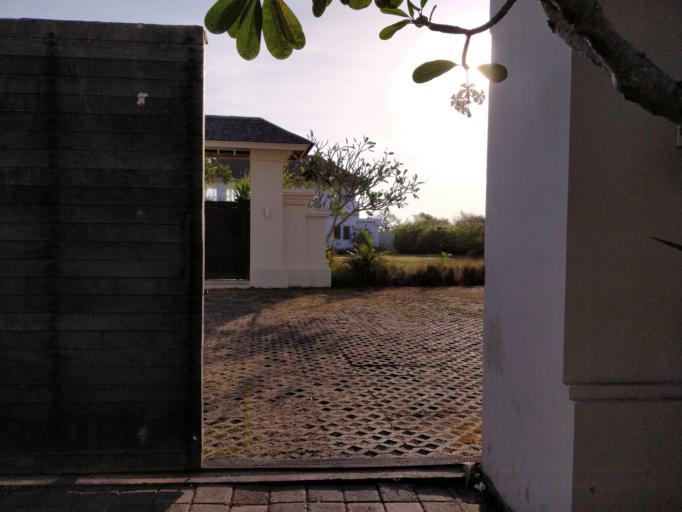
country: ID
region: Bali
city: Lembongan Kawan
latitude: -8.6855
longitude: 115.4296
